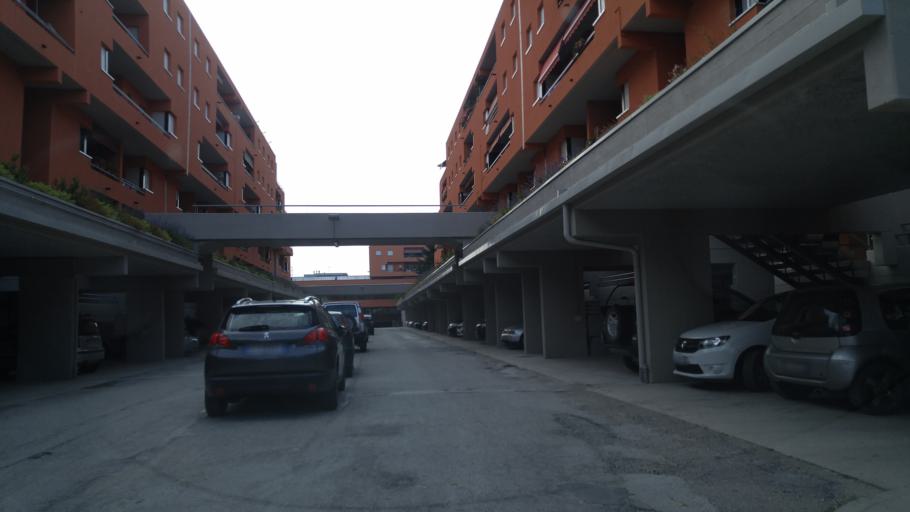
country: IT
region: The Marches
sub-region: Provincia di Pesaro e Urbino
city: Centinarola
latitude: 43.8321
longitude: 13.0043
